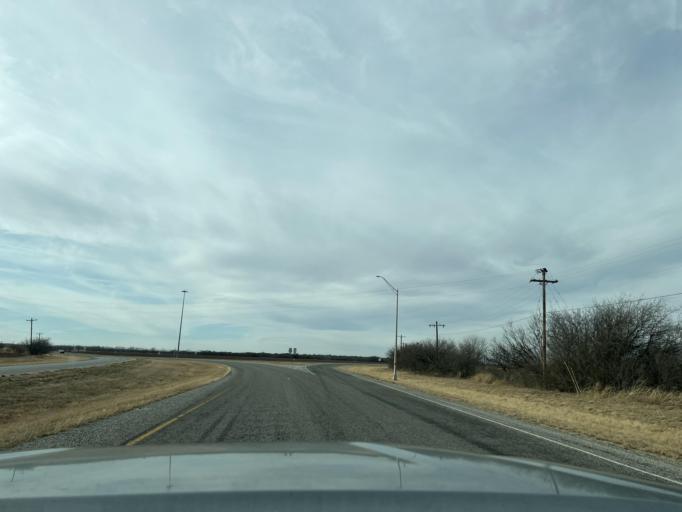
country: US
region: Texas
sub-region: Jones County
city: Stamford
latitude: 32.7665
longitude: -99.5870
